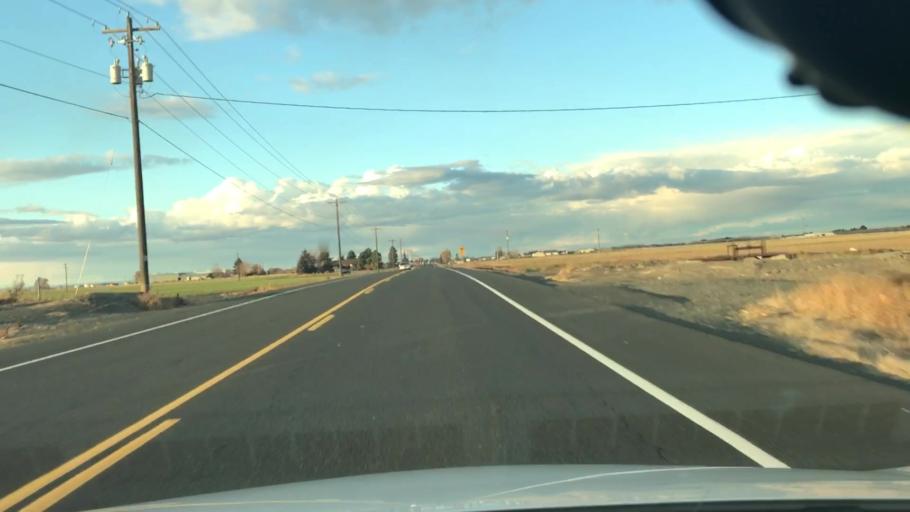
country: US
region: Washington
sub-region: Grant County
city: Moses Lake
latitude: 47.1132
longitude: -119.2359
